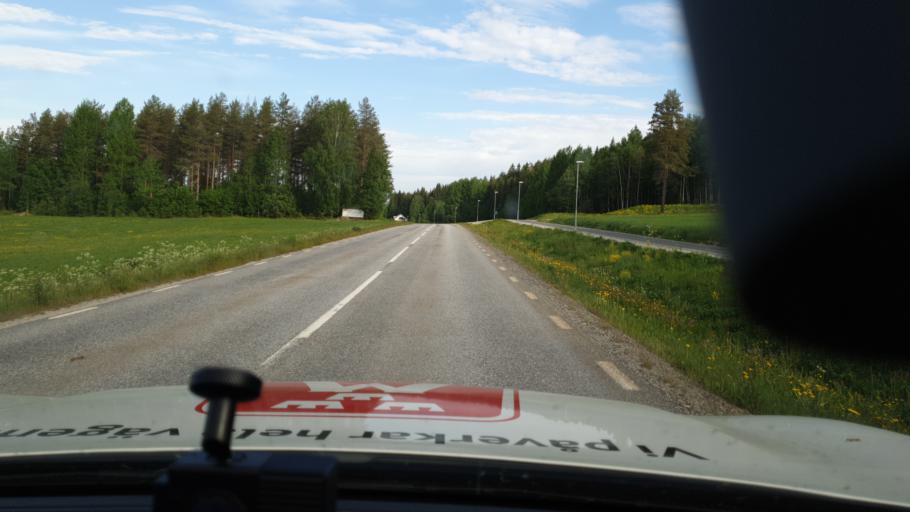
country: SE
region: Vaesterbotten
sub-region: Bjurholms Kommun
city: Bjurholm
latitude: 64.2379
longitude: 19.3404
